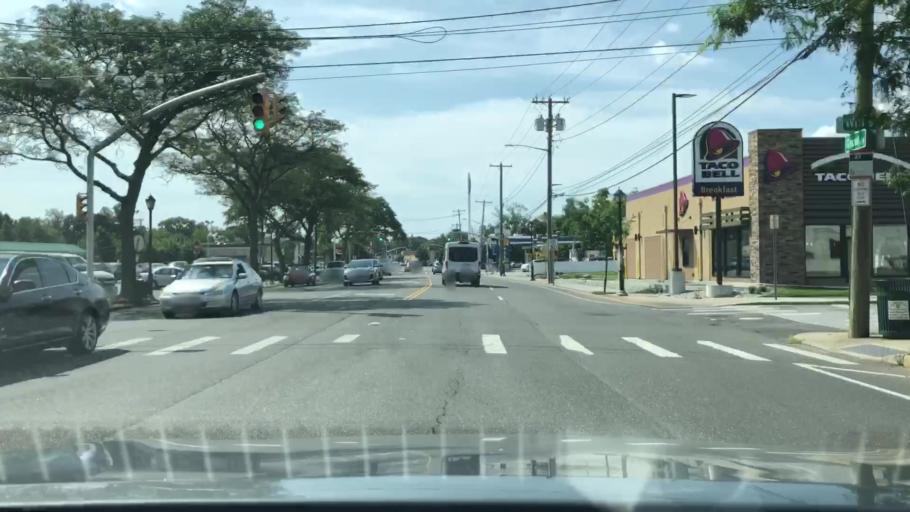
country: US
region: New York
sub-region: Nassau County
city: South Hempstead
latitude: 40.6821
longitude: -73.6152
